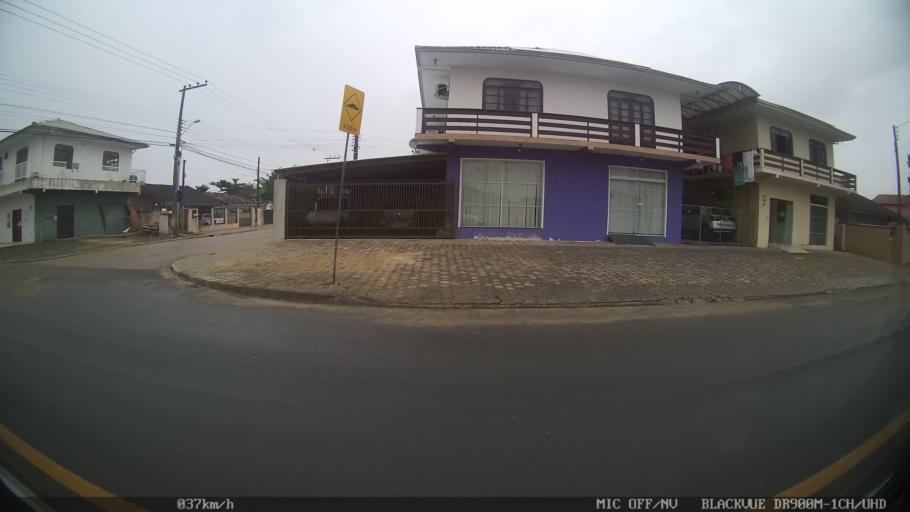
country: BR
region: Santa Catarina
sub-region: Joinville
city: Joinville
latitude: -26.2686
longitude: -48.8010
